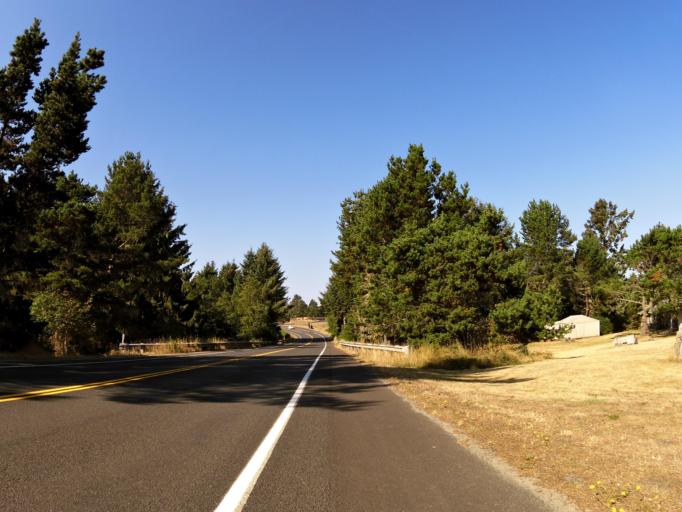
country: US
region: Oregon
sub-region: Clatsop County
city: Gearhart
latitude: 46.0498
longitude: -123.9181
